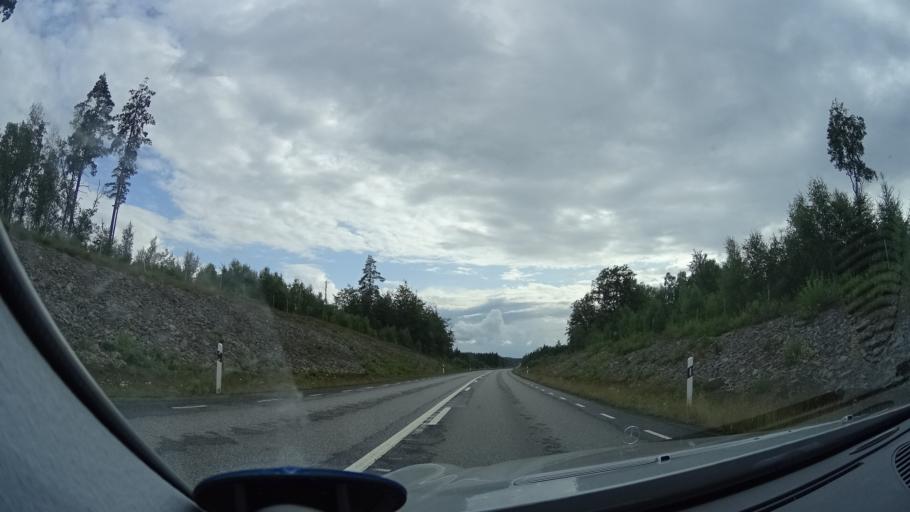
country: SE
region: Blekinge
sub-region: Karlshamns Kommun
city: Svangsta
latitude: 56.2742
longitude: 14.8602
